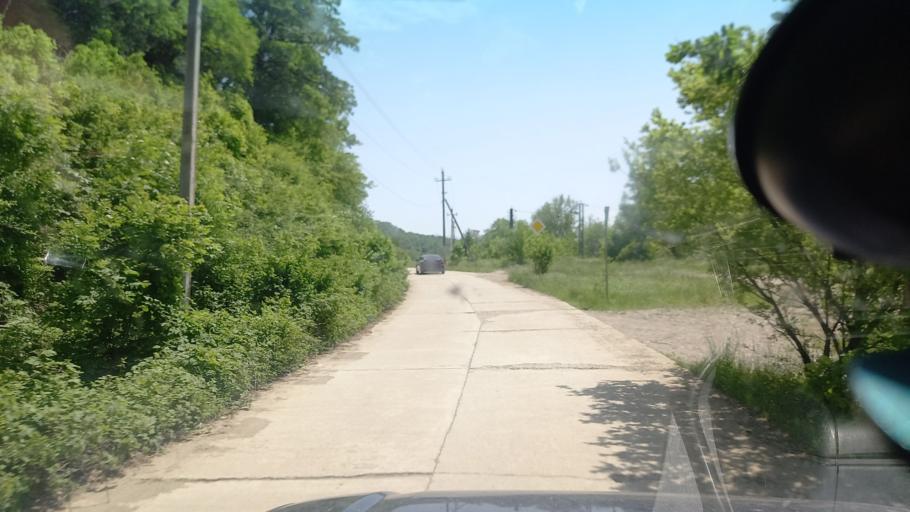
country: RU
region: Krasnodarskiy
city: Tuapse
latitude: 44.2424
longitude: 39.2402
